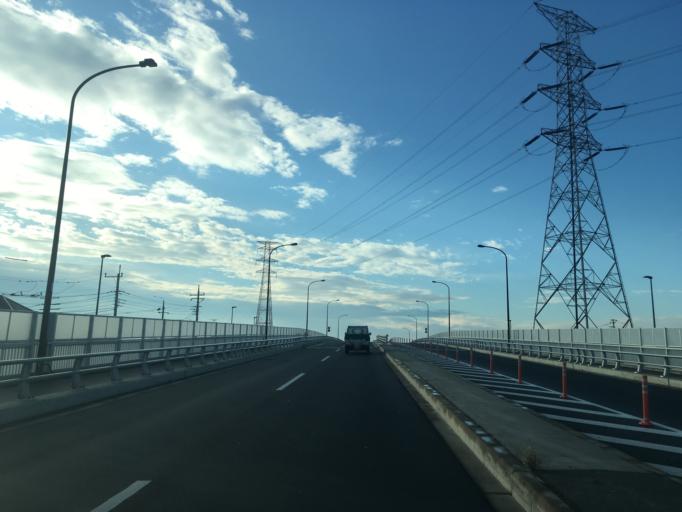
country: JP
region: Tokyo
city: Kokubunji
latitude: 35.7007
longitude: 139.4603
